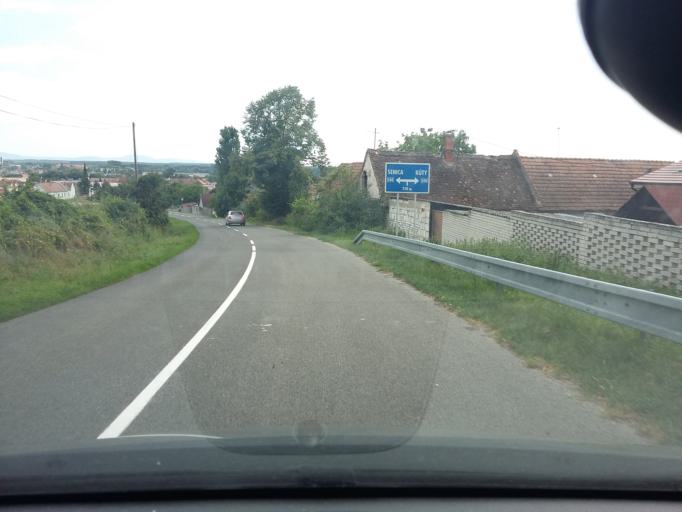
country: SK
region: Trnavsky
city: Gbely
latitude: 48.6502
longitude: 17.1422
